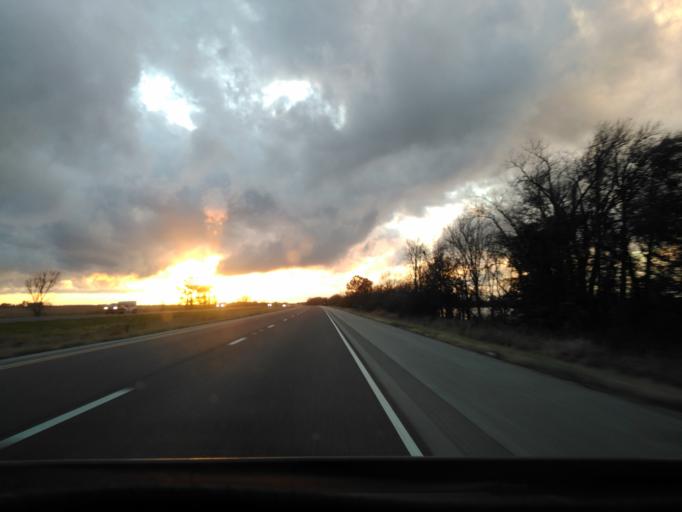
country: US
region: Illinois
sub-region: Fayette County
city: Saint Elmo
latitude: 38.9939
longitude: -88.9203
